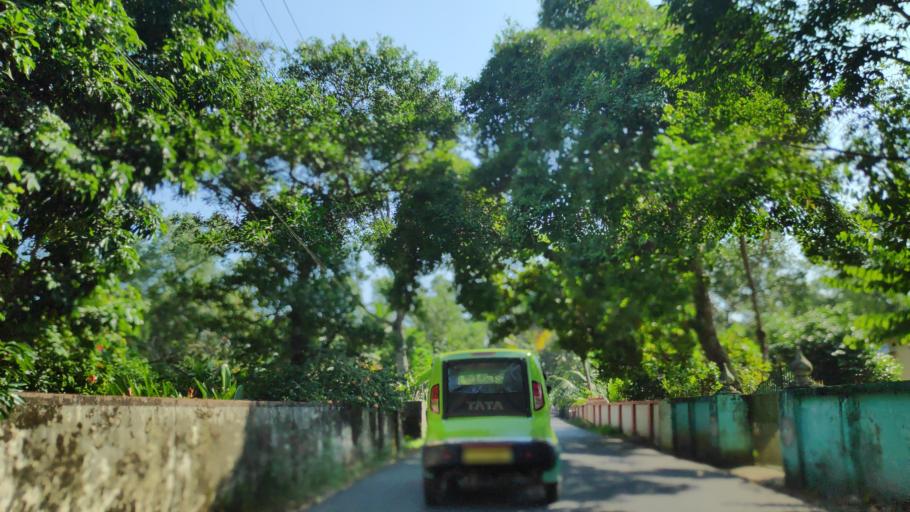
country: IN
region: Kerala
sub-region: Alappuzha
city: Alleppey
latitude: 9.5734
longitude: 76.3167
